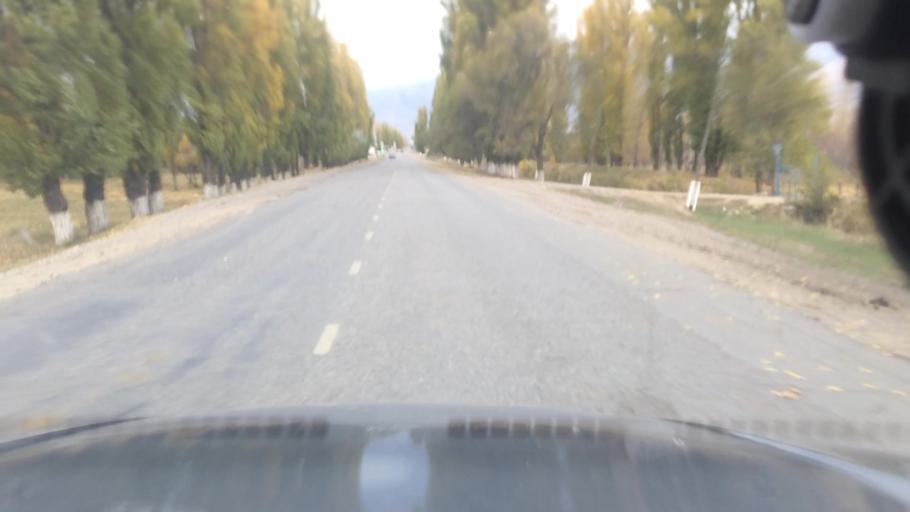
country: KG
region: Ysyk-Koel
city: Tyup
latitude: 42.7357
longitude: 78.3506
